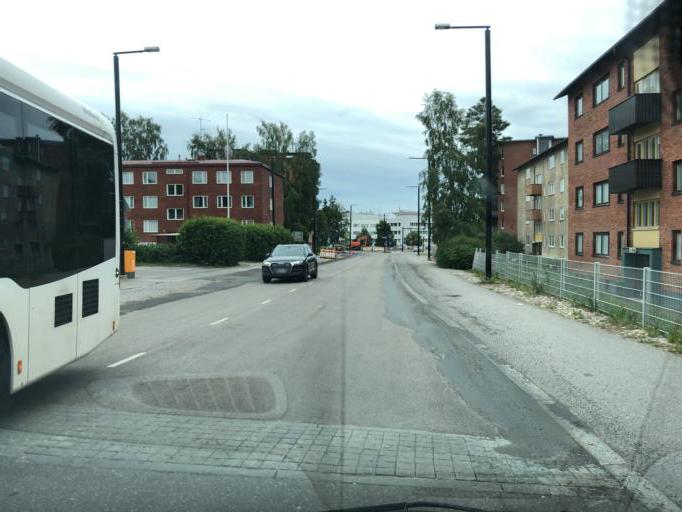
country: FI
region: Uusimaa
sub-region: Helsinki
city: Vantaa
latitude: 60.3010
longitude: 25.0401
